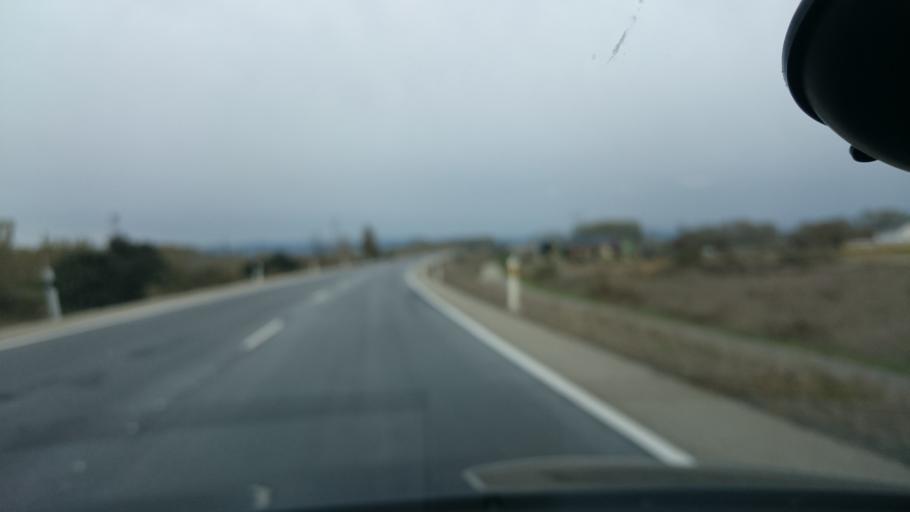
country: ES
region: Castille and Leon
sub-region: Provincia de Leon
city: Priaranza del Bierzo
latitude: 42.5417
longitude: -6.6613
